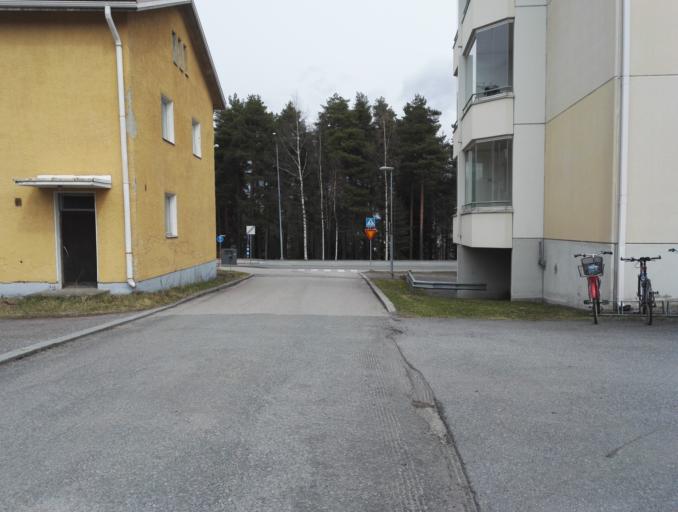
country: FI
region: Pirkanmaa
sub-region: Tampere
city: Tampere
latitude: 61.4923
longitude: 23.8056
